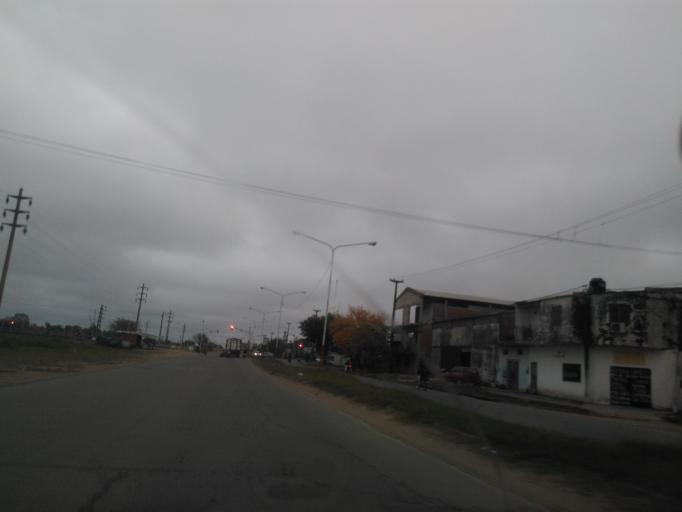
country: AR
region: Chaco
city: Resistencia
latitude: -27.4752
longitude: -59.0026
